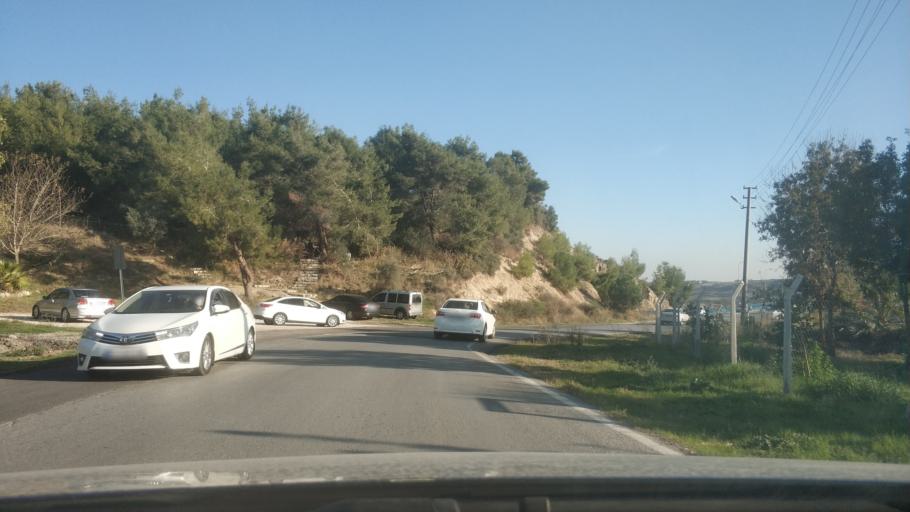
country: TR
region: Adana
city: Adana
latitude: 37.1052
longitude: 35.2984
